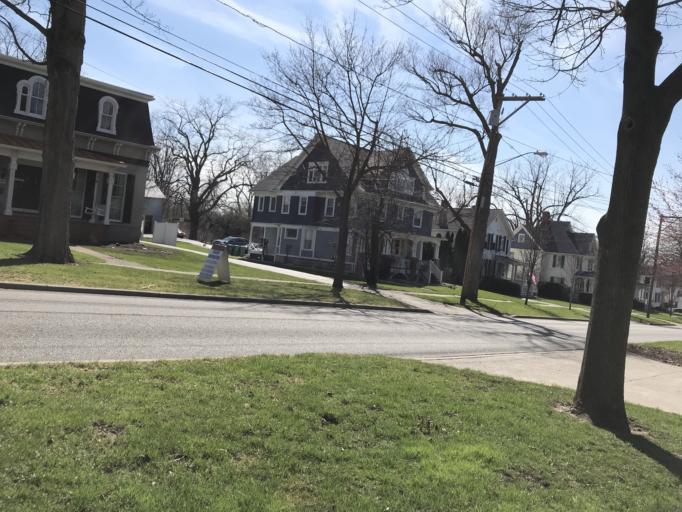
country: US
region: New York
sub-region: Livingston County
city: Geneseo
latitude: 42.7956
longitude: -77.8103
